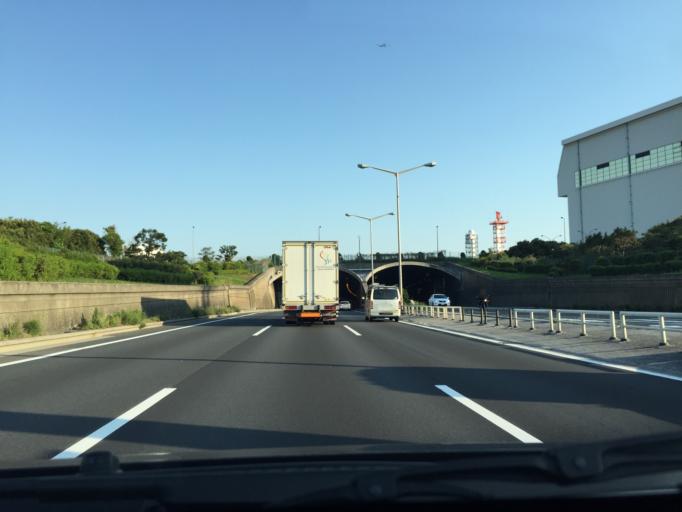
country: JP
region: Kanagawa
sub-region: Kawasaki-shi
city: Kawasaki
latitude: 35.5371
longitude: 139.7949
